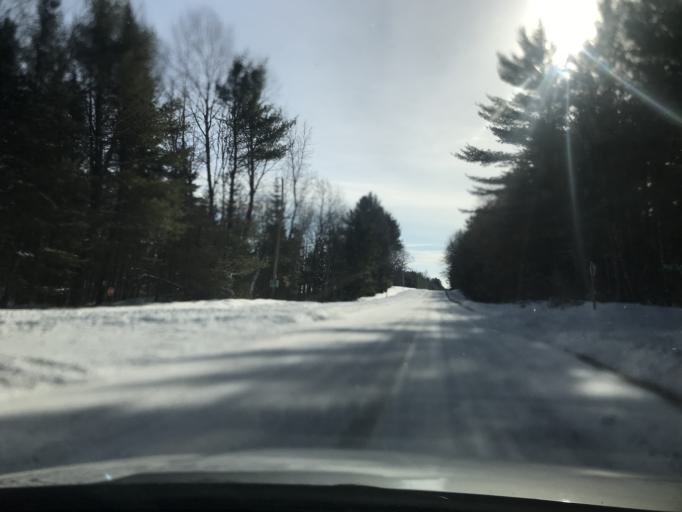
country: US
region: Wisconsin
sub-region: Oconto County
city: Gillett
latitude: 45.1340
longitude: -88.2497
